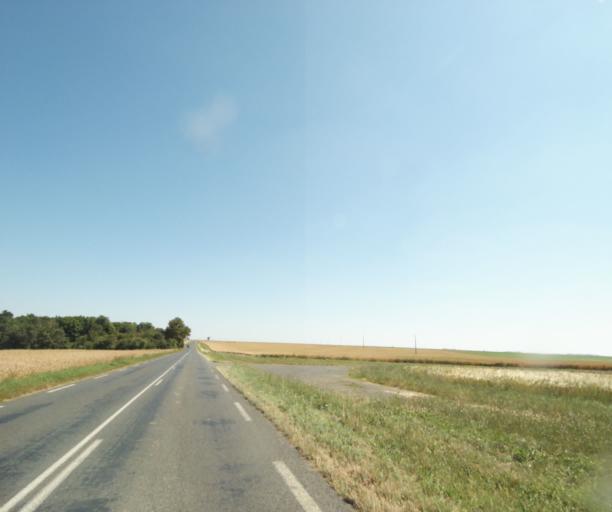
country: FR
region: Ile-de-France
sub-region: Departement de Seine-et-Marne
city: La Chapelle-la-Reine
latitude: 48.2958
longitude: 2.5746
